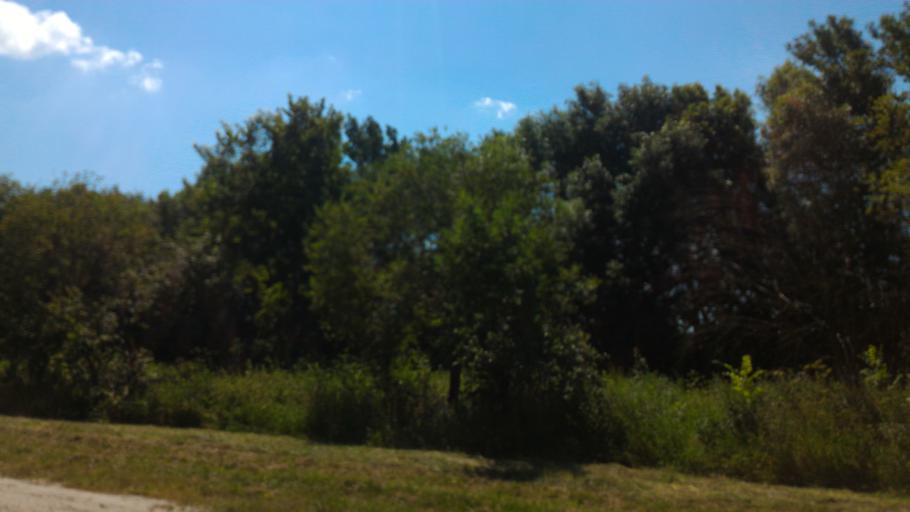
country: RU
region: Rjazan
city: Bagramovo
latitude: 54.7231
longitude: 39.4777
